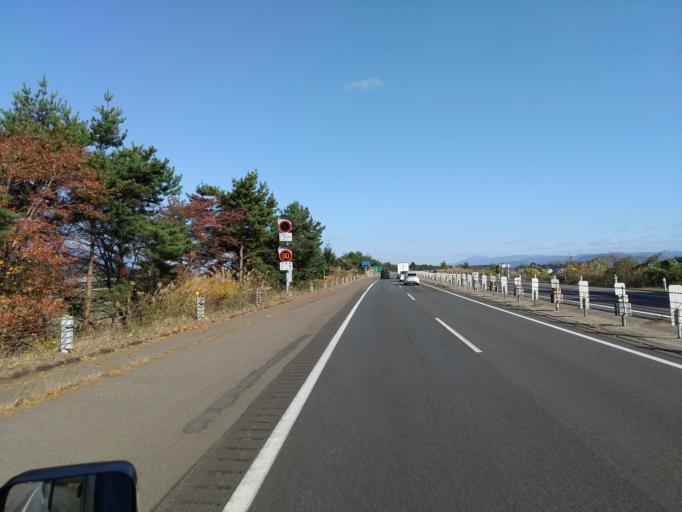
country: JP
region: Iwate
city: Morioka-shi
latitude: 39.5939
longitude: 141.1179
